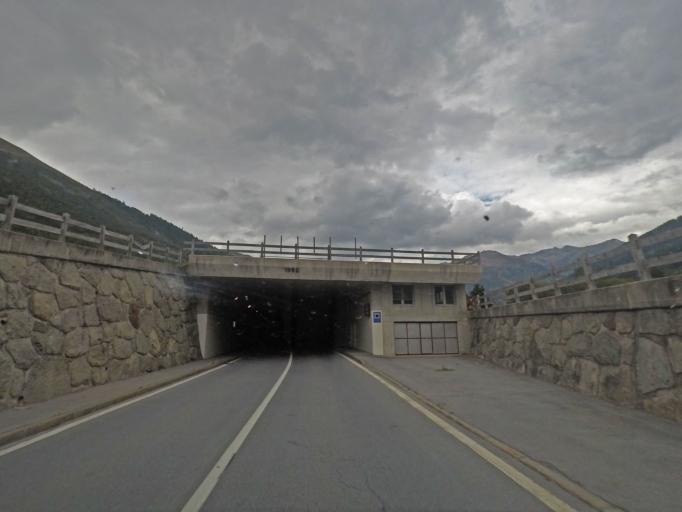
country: IT
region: Piedmont
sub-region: Provincia Verbano-Cusio-Ossola
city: Formazza
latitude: 46.5175
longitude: 8.3277
